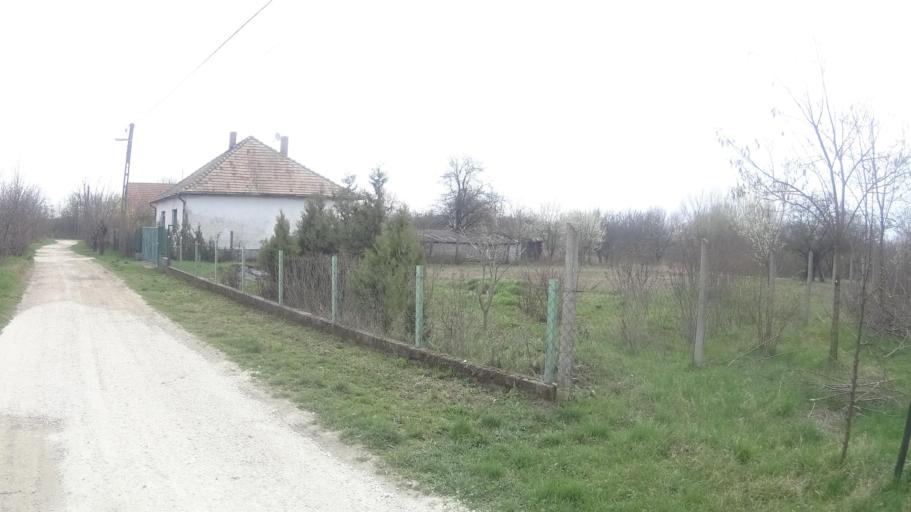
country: HU
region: Fejer
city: Sarosd
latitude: 46.9745
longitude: 18.6456
